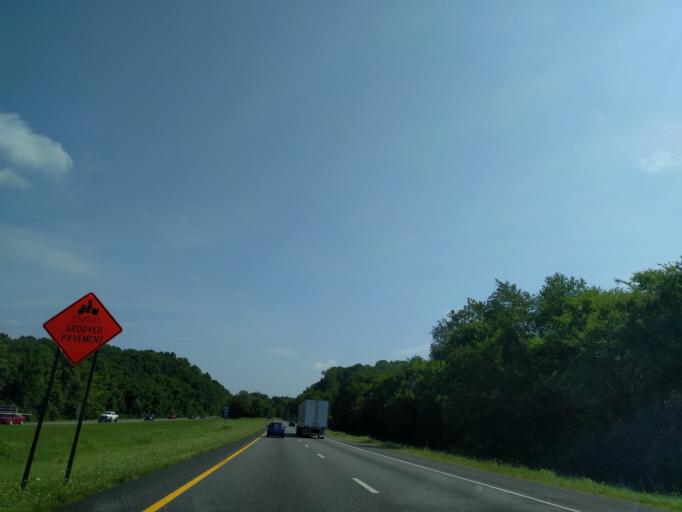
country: US
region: Tennessee
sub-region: Robertson County
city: Cross Plains
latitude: 36.5788
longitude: -86.6131
